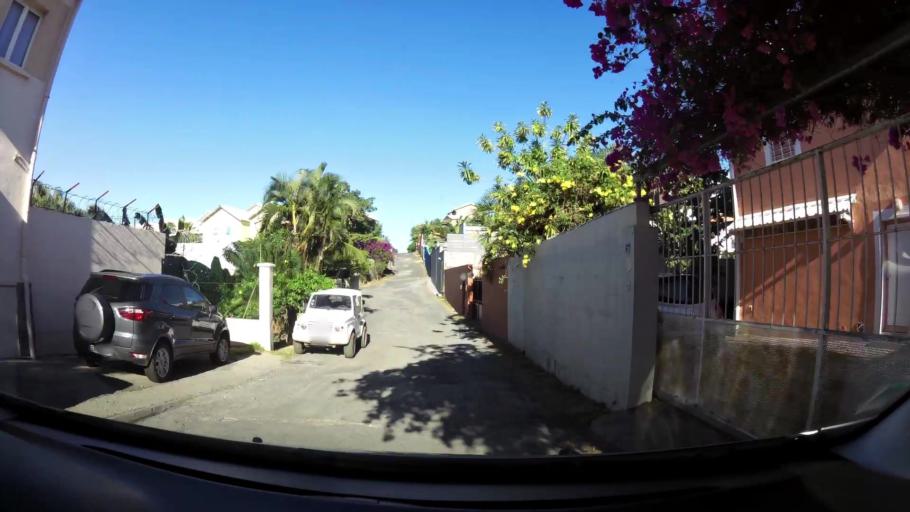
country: YT
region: Mamoudzou
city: Mamoudzou
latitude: -12.7548
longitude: 45.2281
